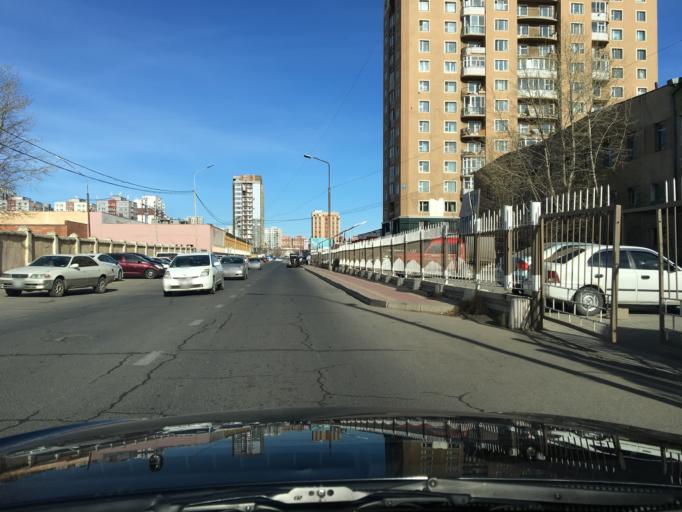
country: MN
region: Ulaanbaatar
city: Ulaanbaatar
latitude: 47.8963
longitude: 106.9018
